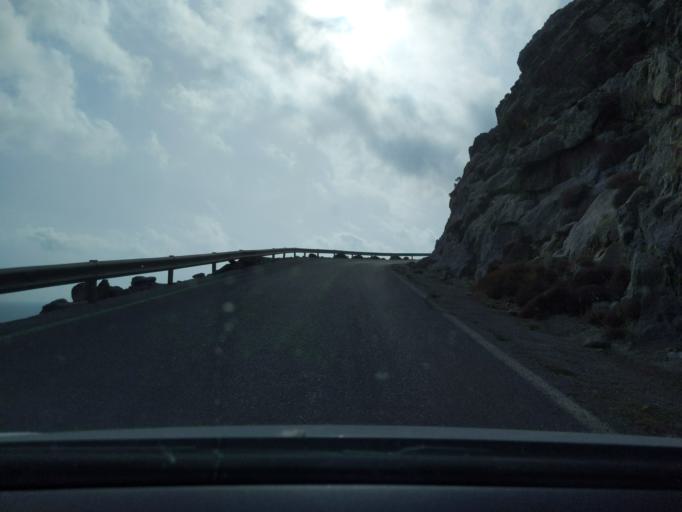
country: GR
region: Crete
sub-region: Nomos Lasithiou
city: Palekastro
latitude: 35.0889
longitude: 26.2669
